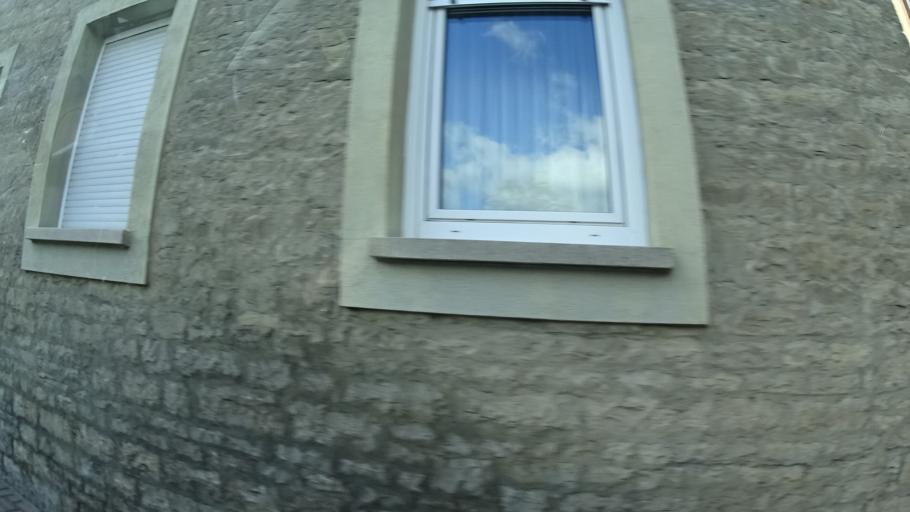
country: DE
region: Bavaria
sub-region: Regierungsbezirk Unterfranken
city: Mainstockheim
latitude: 49.7706
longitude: 10.1522
